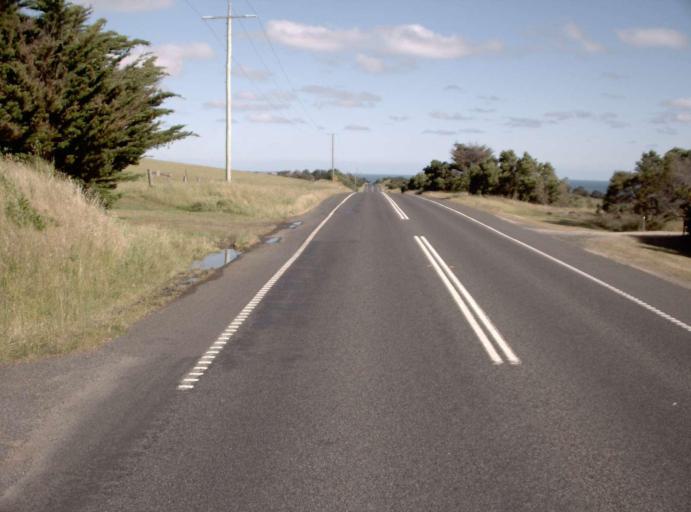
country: AU
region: Victoria
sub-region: Bass Coast
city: North Wonthaggi
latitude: -38.5344
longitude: 145.4540
